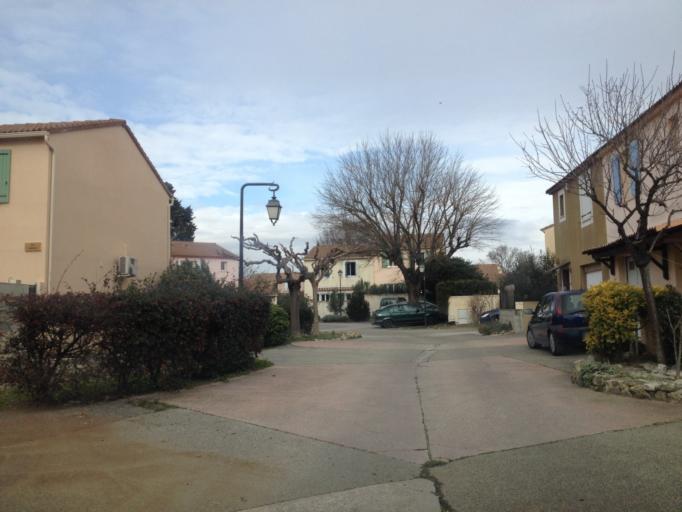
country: FR
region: Provence-Alpes-Cote d'Azur
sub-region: Departement du Vaucluse
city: Orange
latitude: 44.1399
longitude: 4.8217
